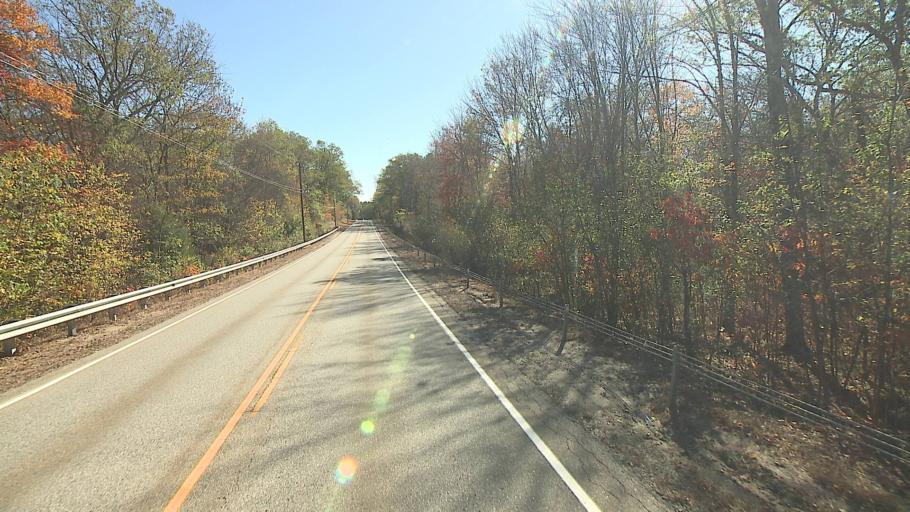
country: US
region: Connecticut
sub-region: Windham County
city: South Woodstock
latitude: 41.8643
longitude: -72.0460
